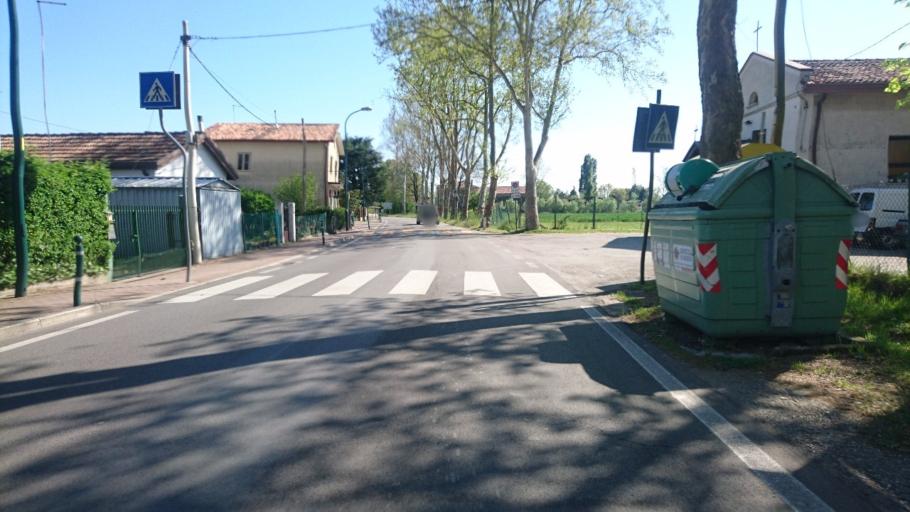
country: IT
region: Veneto
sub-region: Provincia di Venezia
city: Dese
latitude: 45.5232
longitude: 12.2673
